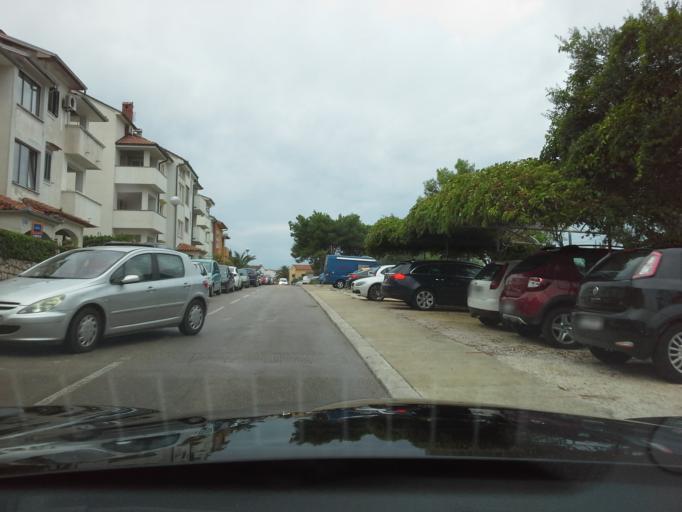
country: HR
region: Primorsko-Goranska
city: Mali Losinj
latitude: 44.5323
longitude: 14.4770
